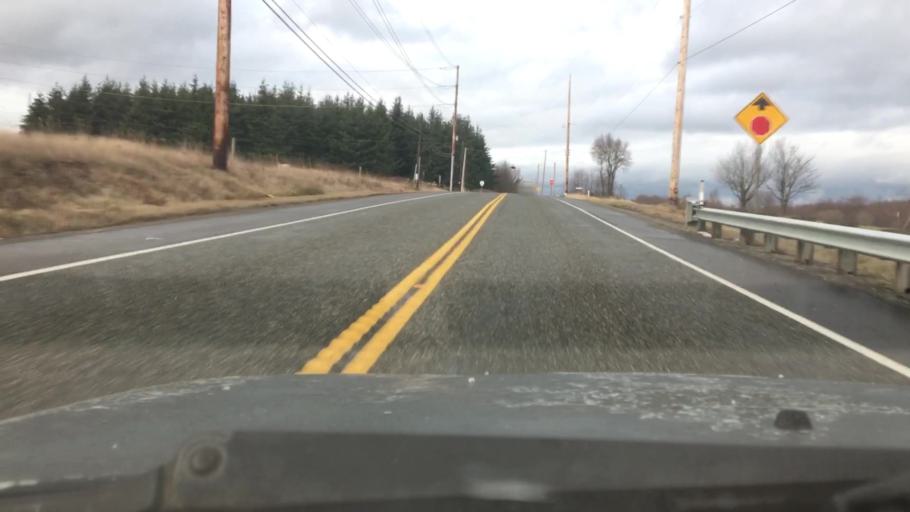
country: US
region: Washington
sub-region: Whatcom County
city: Ferndale
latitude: 48.8471
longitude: -122.6826
